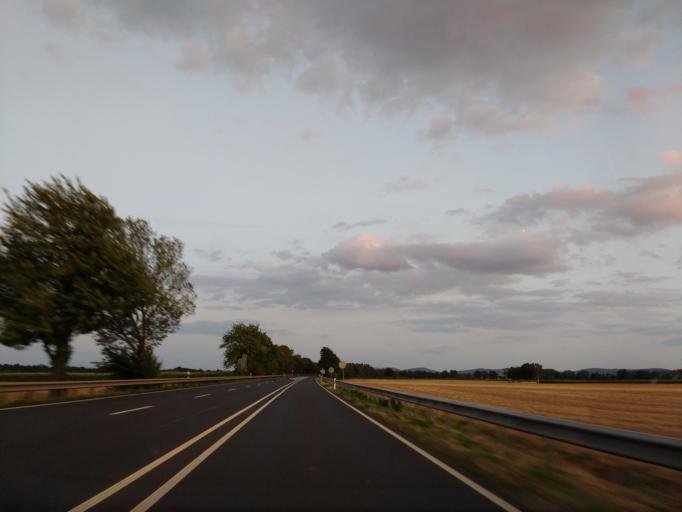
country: DE
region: North Rhine-Westphalia
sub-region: Regierungsbezirk Detmold
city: Petershagen
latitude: 52.3262
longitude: 8.9738
